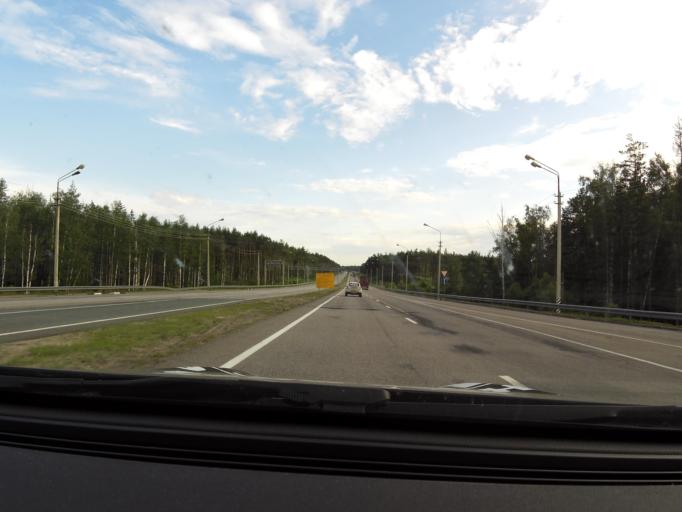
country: RU
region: Vladimir
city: Kameshkovo
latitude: 56.1928
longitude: 40.9511
